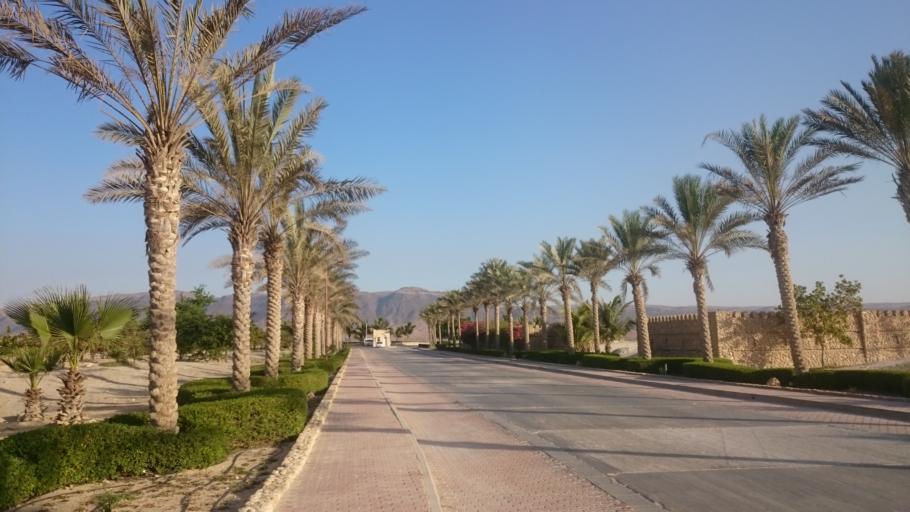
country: OM
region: Zufar
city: Salalah
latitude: 17.0366
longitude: 54.3033
